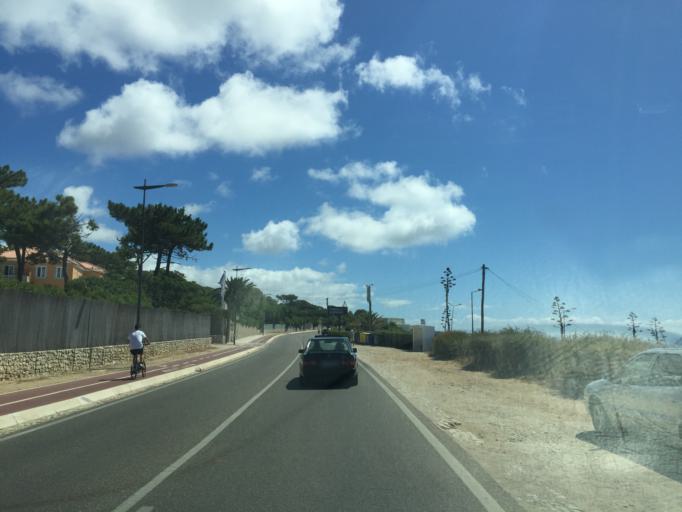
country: PT
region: Lisbon
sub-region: Cascais
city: Cascais
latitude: 38.6955
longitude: -9.4573
